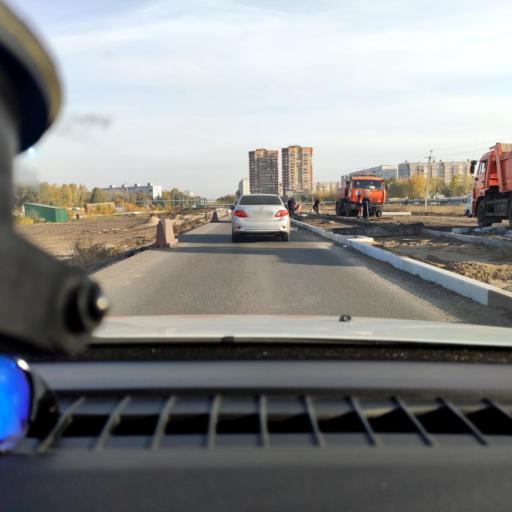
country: RU
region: Samara
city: Samara
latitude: 53.1024
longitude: 50.0778
